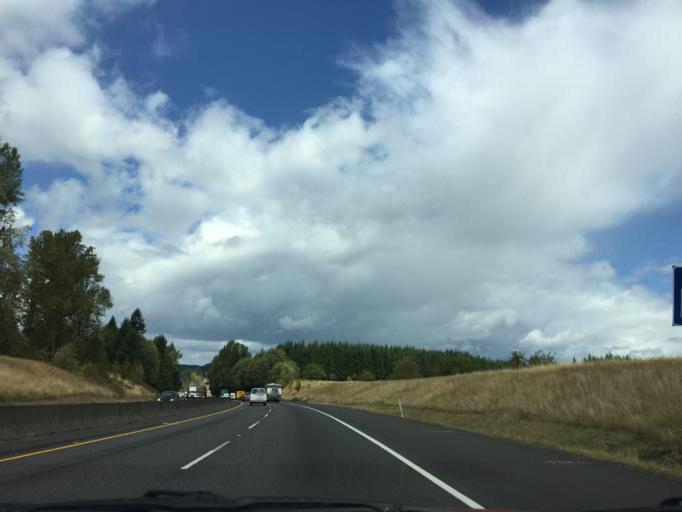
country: US
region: Washington
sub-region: Lewis County
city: Winlock
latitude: 46.4089
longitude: -122.8895
